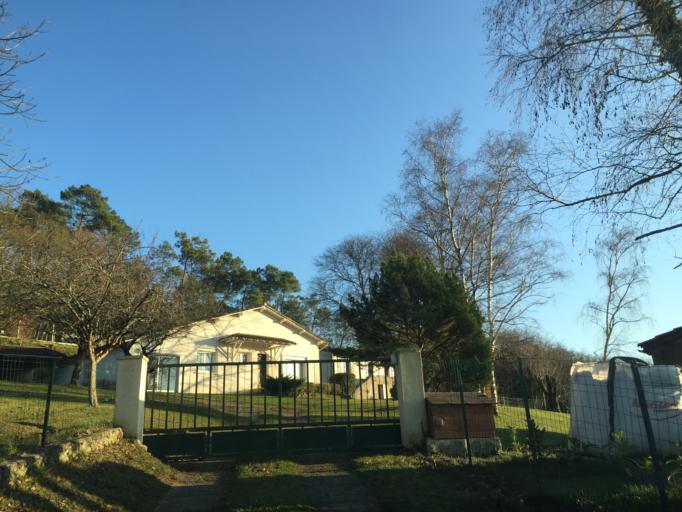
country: FR
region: Poitou-Charentes
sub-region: Departement de la Charente
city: Chalais
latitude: 45.2385
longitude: 0.0378
